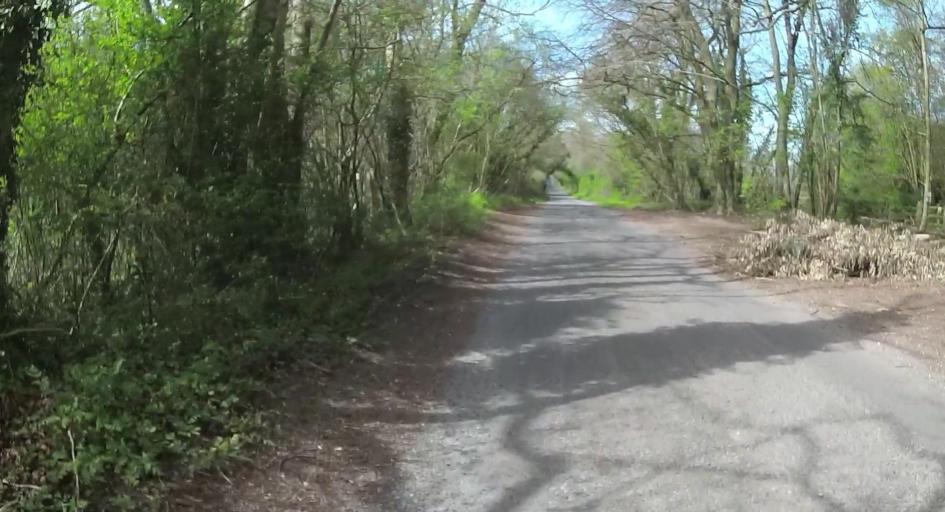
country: GB
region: England
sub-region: Hampshire
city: Chandlers Ford
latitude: 51.0609
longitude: -1.4118
